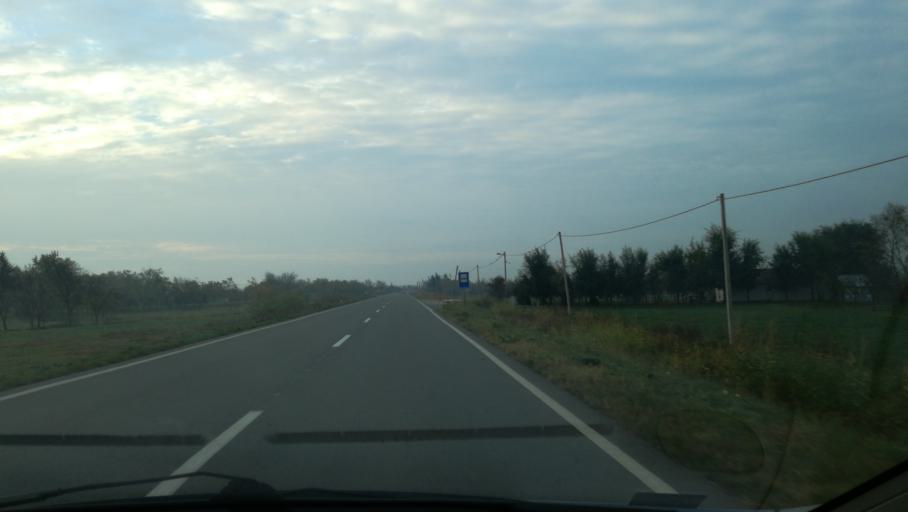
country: RS
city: Banatska Topola
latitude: 45.6895
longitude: 20.4227
